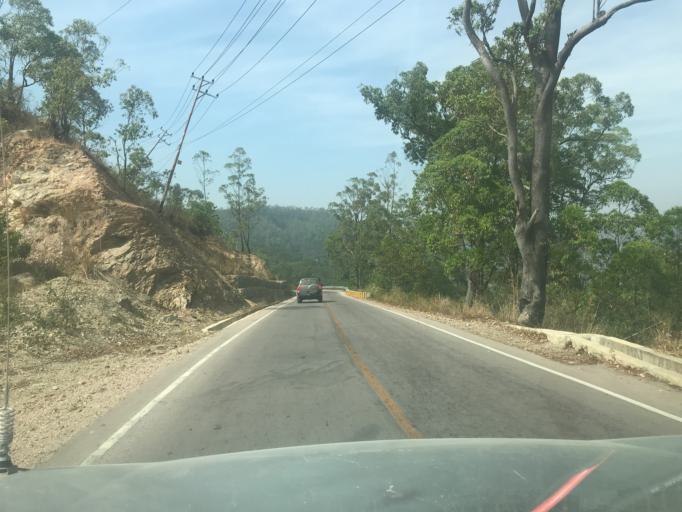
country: TL
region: Aileu
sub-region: Aileu Villa
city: Aileu
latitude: -8.6632
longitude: 125.5594
